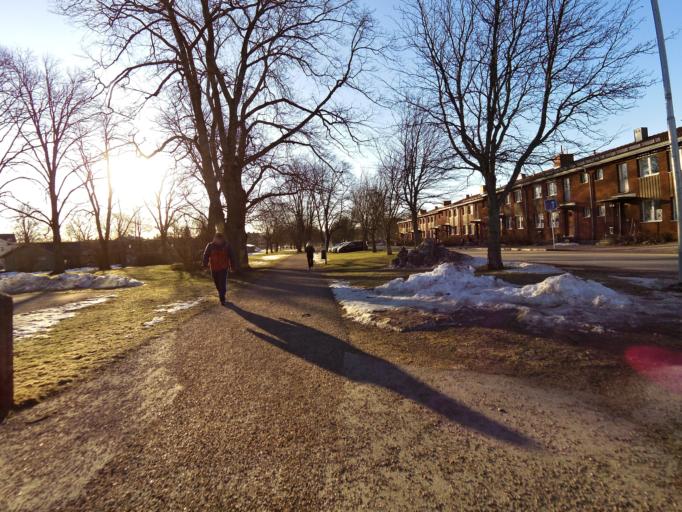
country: SE
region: Gaevleborg
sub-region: Gavle Kommun
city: Gavle
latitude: 60.6654
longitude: 17.1462
